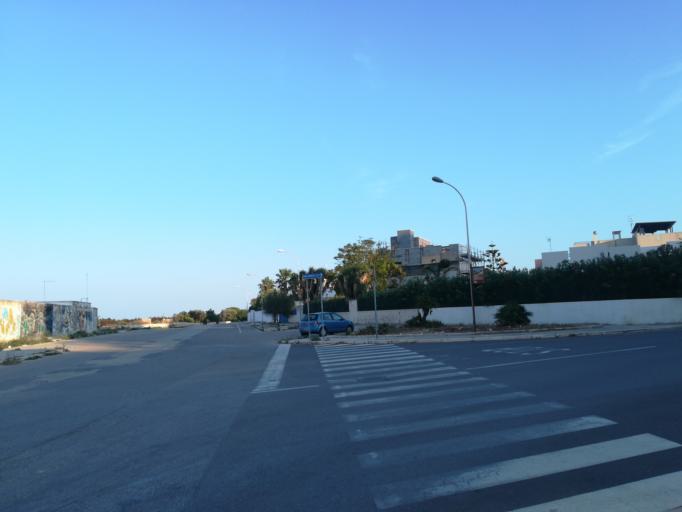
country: IT
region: Apulia
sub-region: Provincia di Bari
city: Polignano a Mare
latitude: 40.9917
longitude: 17.2305
